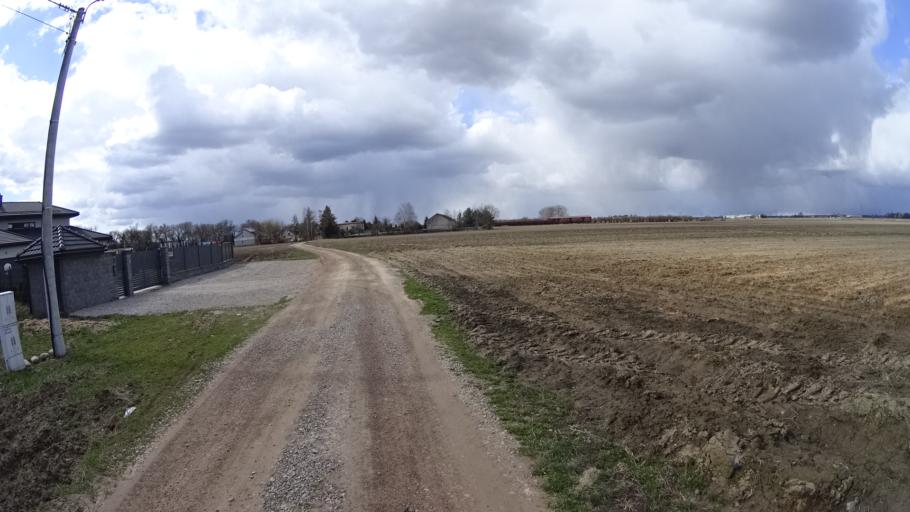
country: PL
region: Masovian Voivodeship
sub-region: Powiat warszawski zachodni
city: Jozefow
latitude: 52.2138
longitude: 20.7050
